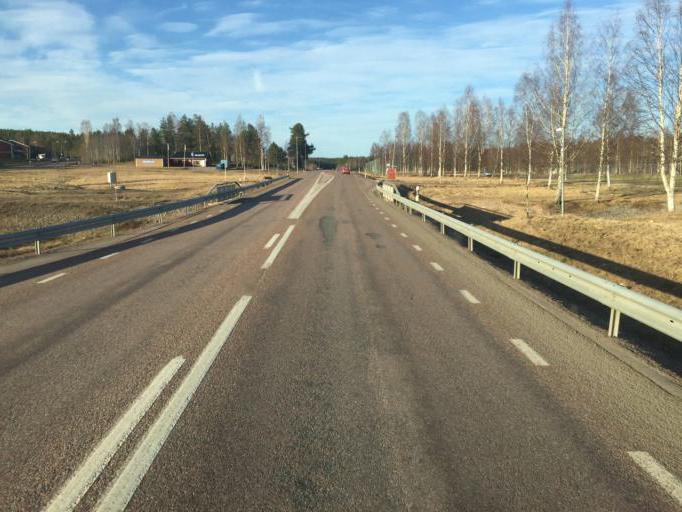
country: SE
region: Dalarna
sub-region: Gagnefs Kommun
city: Mockfjard
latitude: 60.5096
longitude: 14.9647
